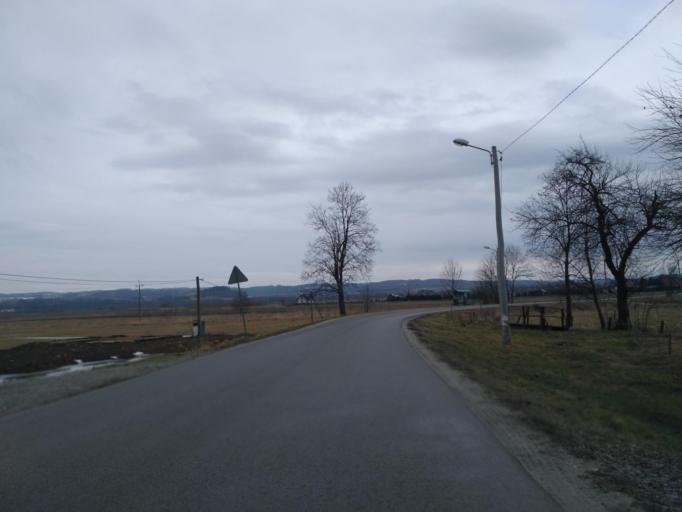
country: PL
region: Subcarpathian Voivodeship
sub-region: Powiat rzeszowski
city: Dynow
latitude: 49.8148
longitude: 22.2735
